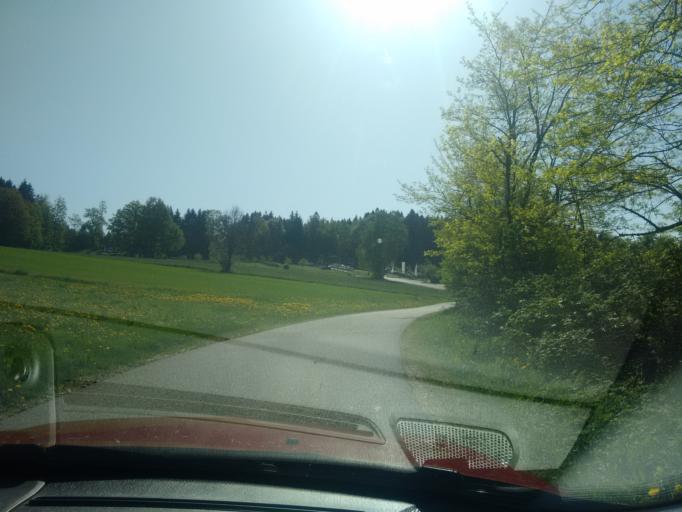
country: DE
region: Bavaria
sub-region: Lower Bavaria
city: Obernzell
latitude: 48.4496
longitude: 13.6645
